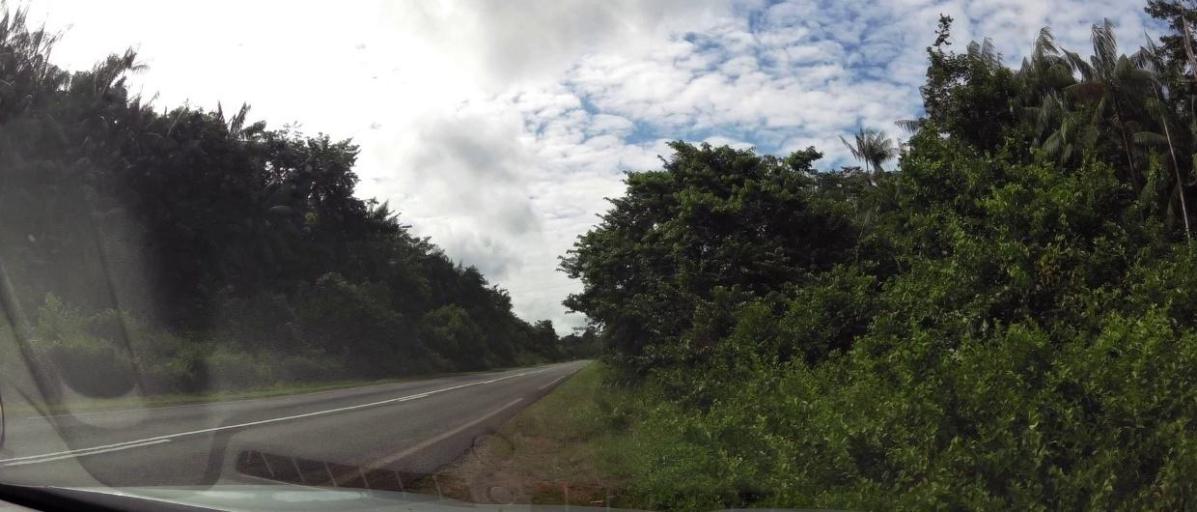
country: GF
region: Guyane
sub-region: Guyane
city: Sinnamary
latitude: 5.3717
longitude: -52.9654
